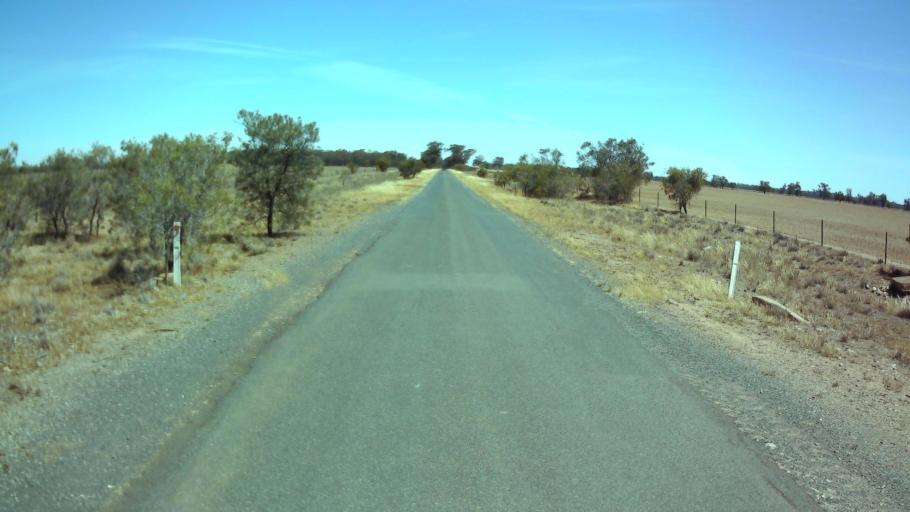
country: AU
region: New South Wales
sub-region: Weddin
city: Grenfell
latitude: -33.8957
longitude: 147.6873
